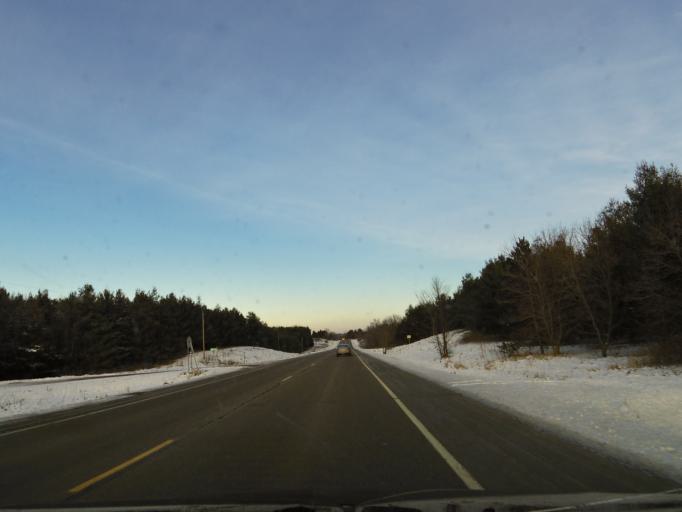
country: US
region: Minnesota
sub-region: Chisago County
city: Shafer
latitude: 45.3697
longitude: -92.7104
